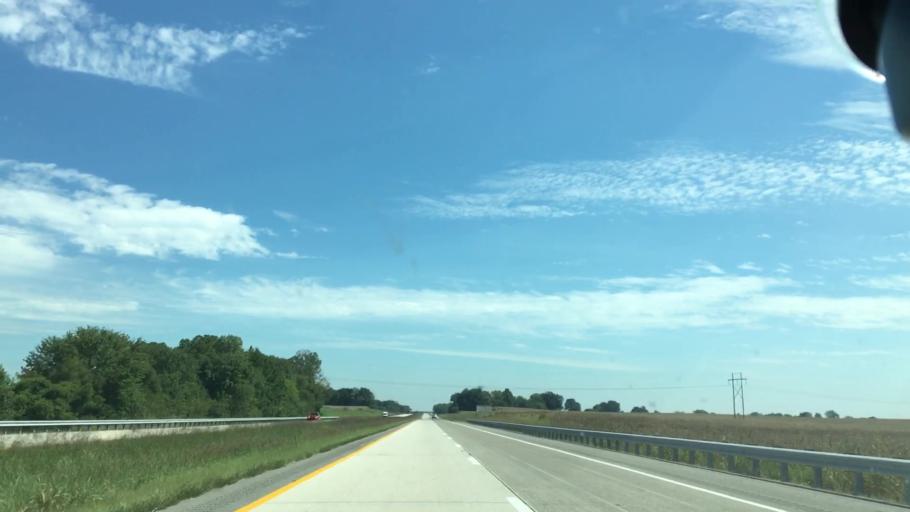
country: US
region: Kentucky
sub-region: Henderson County
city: Henderson
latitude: 37.7999
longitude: -87.5133
